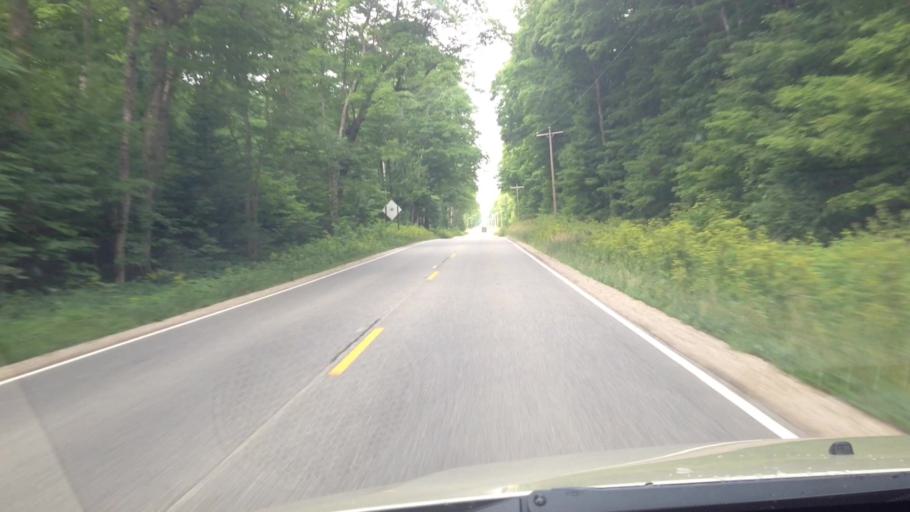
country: US
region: Michigan
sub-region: Mackinac County
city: Saint Ignace
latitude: 46.0570
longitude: -85.1233
